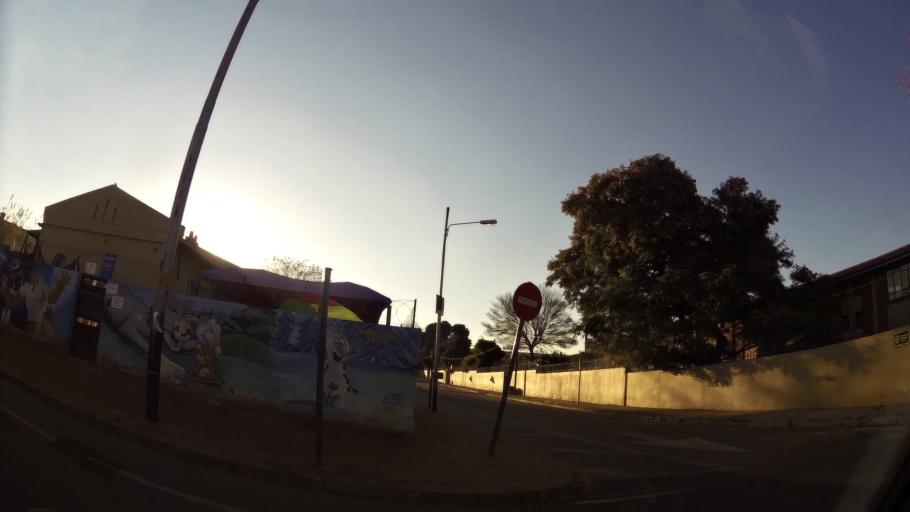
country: ZA
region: Gauteng
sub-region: Ekurhuleni Metropolitan Municipality
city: Germiston
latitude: -26.2686
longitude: 28.1234
